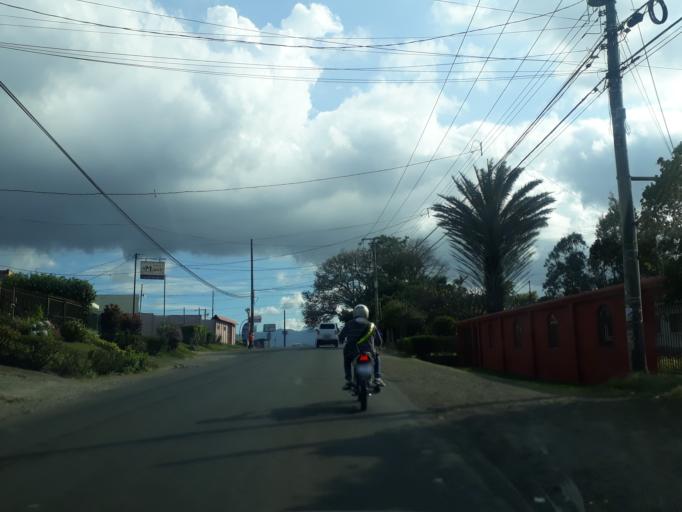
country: CR
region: San Jose
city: Purral
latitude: 9.9698
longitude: -84.0341
